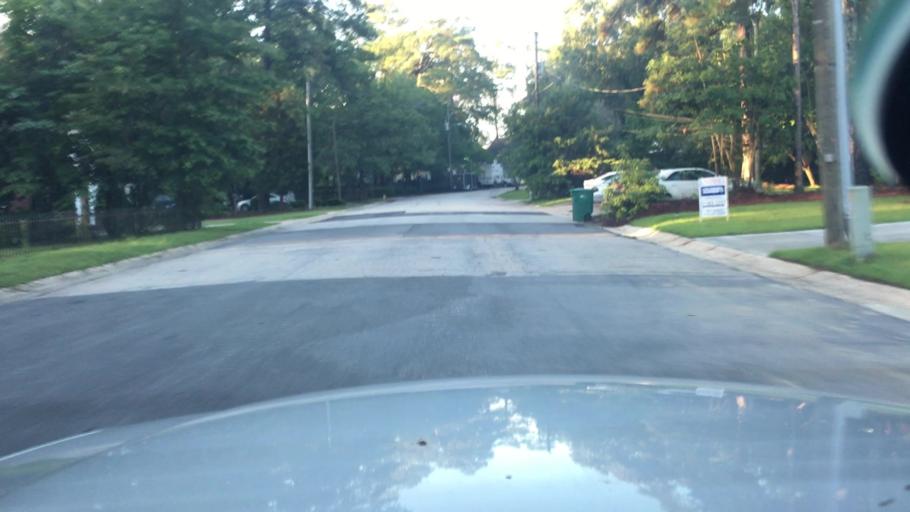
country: US
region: North Carolina
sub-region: Cumberland County
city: Fayetteville
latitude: 35.0689
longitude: -78.9172
